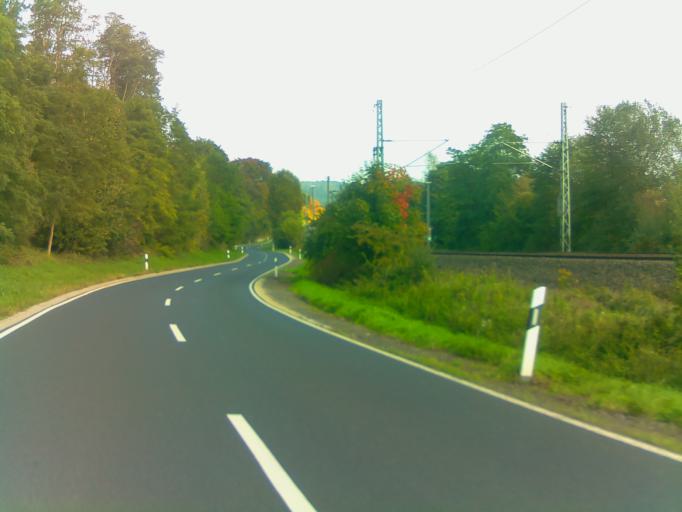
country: DE
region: Thuringia
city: Lauchroden
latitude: 51.0109
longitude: 10.1092
